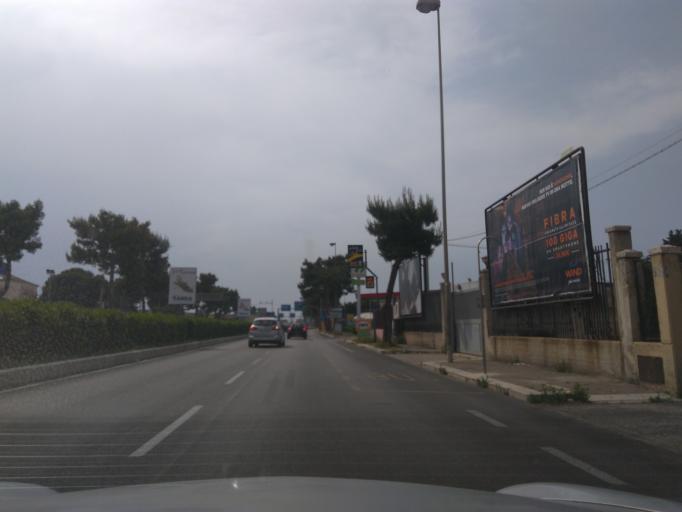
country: IT
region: Apulia
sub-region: Provincia di Bari
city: San Paolo
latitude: 41.1337
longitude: 16.8201
